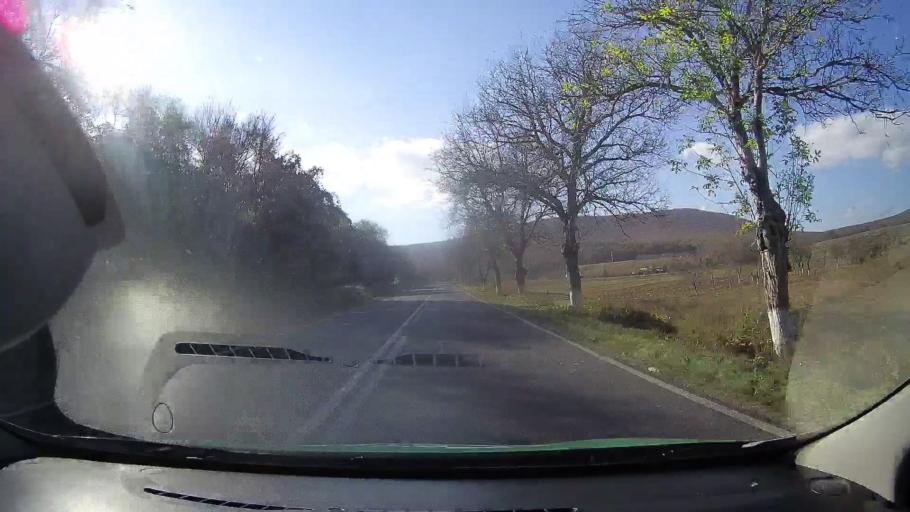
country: RO
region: Tulcea
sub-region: Oras Babadag
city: Babadag
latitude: 44.8763
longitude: 28.6909
